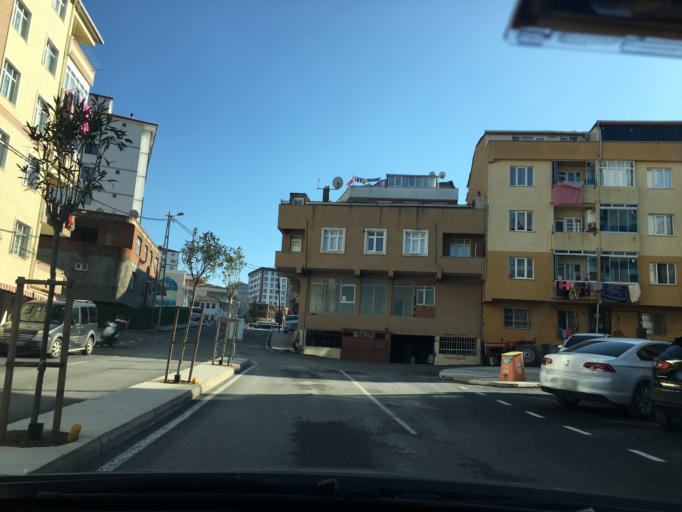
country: TR
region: Istanbul
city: Icmeler
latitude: 40.8683
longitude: 29.3028
